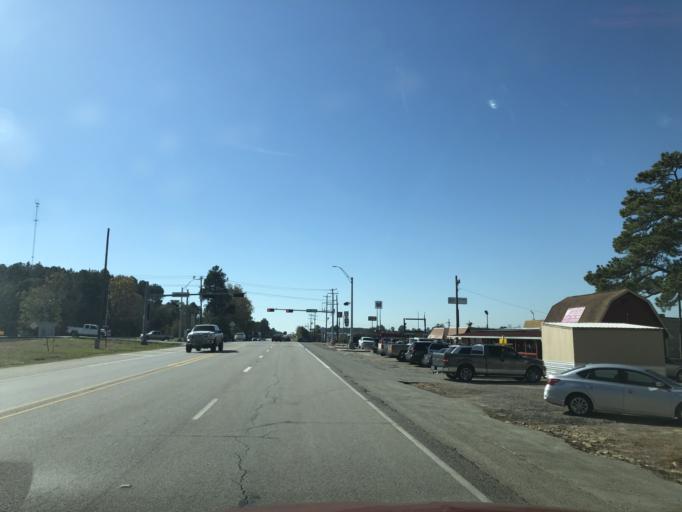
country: US
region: Texas
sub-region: Montgomery County
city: Splendora
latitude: 30.2342
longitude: -95.1621
